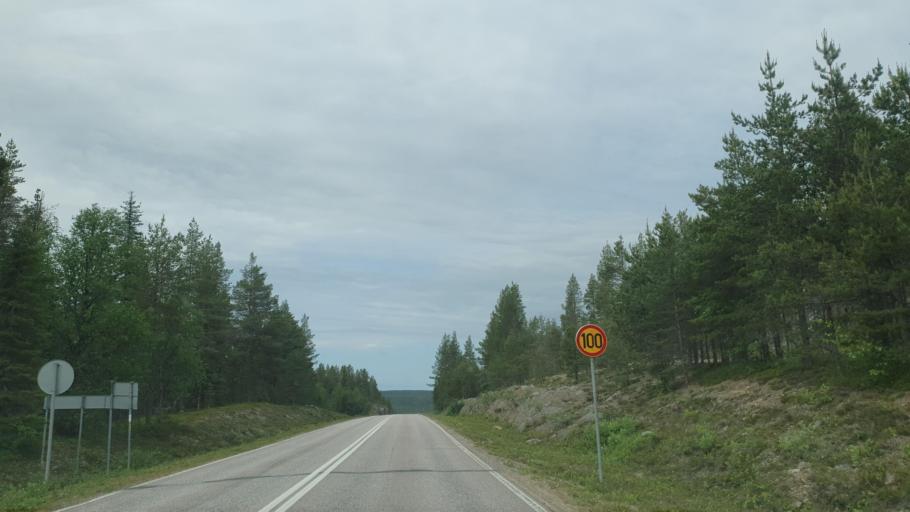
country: FI
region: Lapland
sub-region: Tunturi-Lappi
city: Muonio
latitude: 67.8610
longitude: 24.1019
